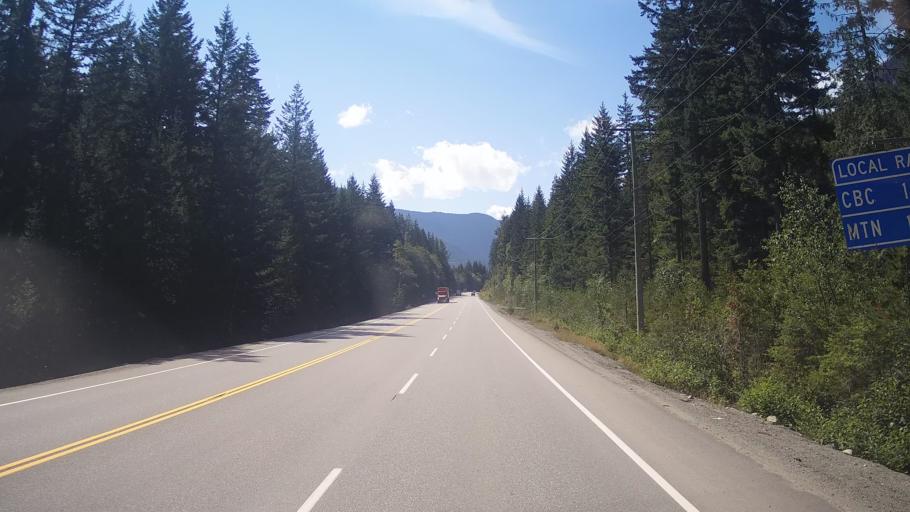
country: CA
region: British Columbia
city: Whistler
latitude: 50.2059
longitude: -122.8822
